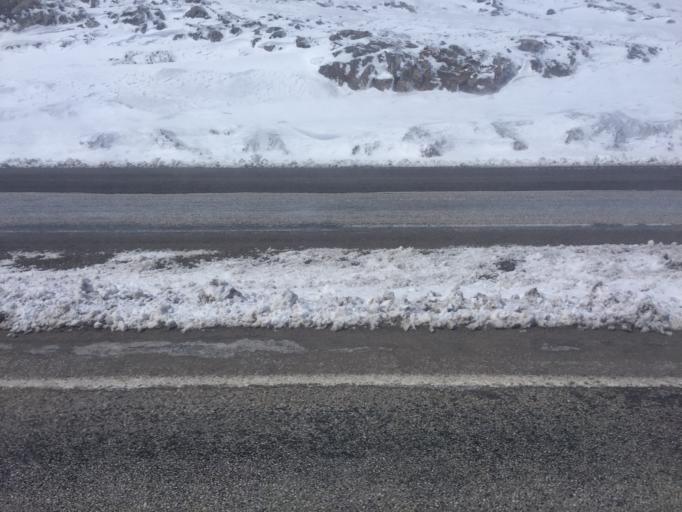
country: TR
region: Kahramanmaras
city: Goksun
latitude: 38.1922
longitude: 36.4569
